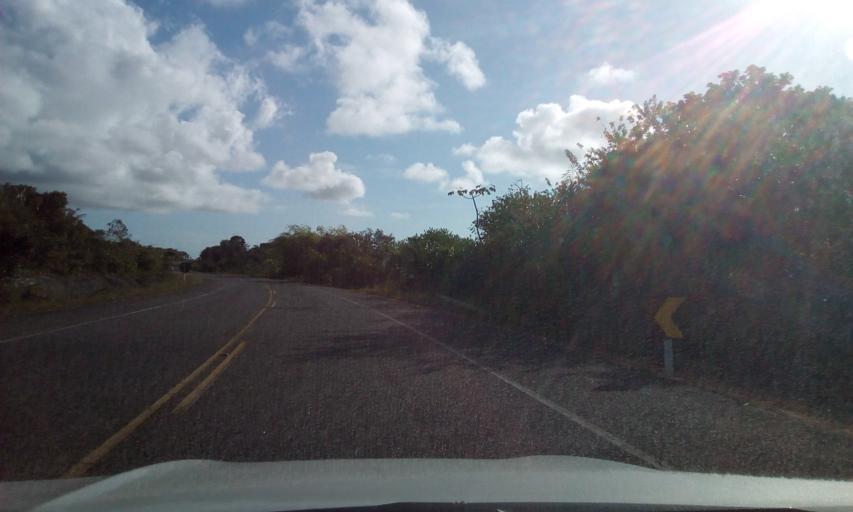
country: BR
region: Bahia
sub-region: Conde
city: Conde
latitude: -12.0827
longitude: -37.7657
